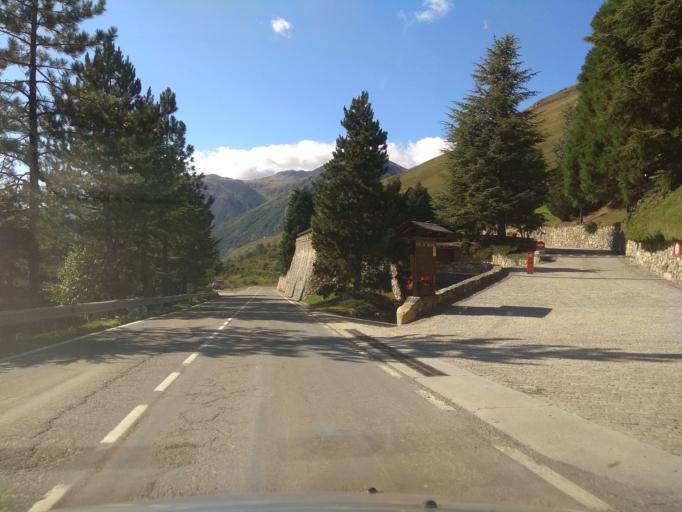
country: ES
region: Catalonia
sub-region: Provincia de Lleida
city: Vielha
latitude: 42.7028
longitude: 0.9288
